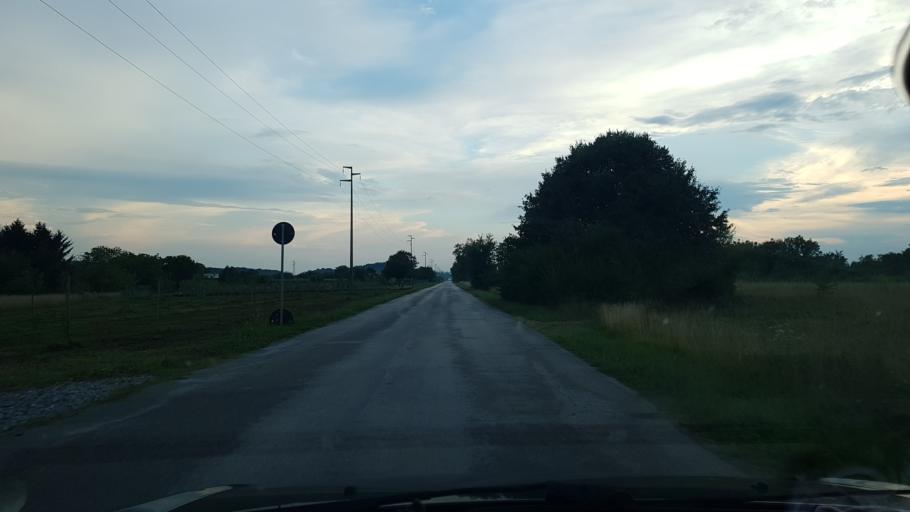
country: IT
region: Friuli Venezia Giulia
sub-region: Provincia di Gorizia
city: Savogna d'Isonzo
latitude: 45.9229
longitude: 13.5655
